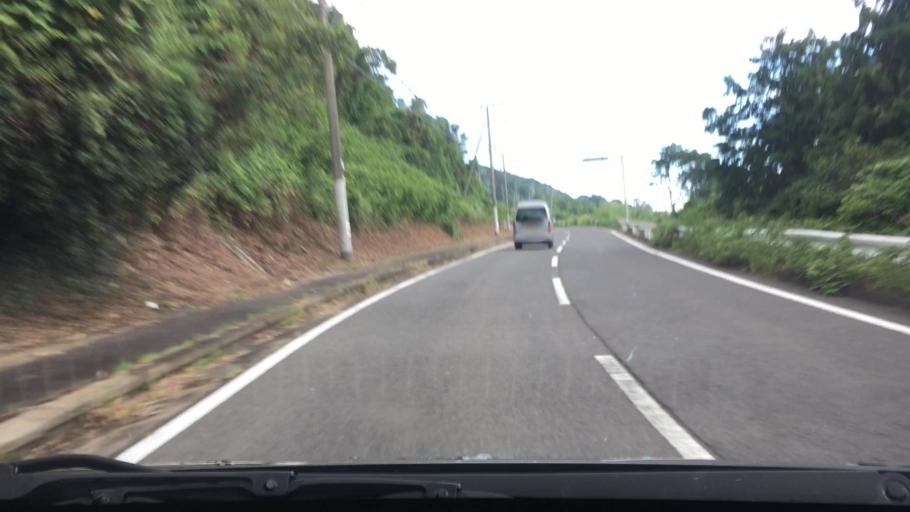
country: JP
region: Nagasaki
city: Togitsu
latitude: 32.8679
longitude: 129.6808
